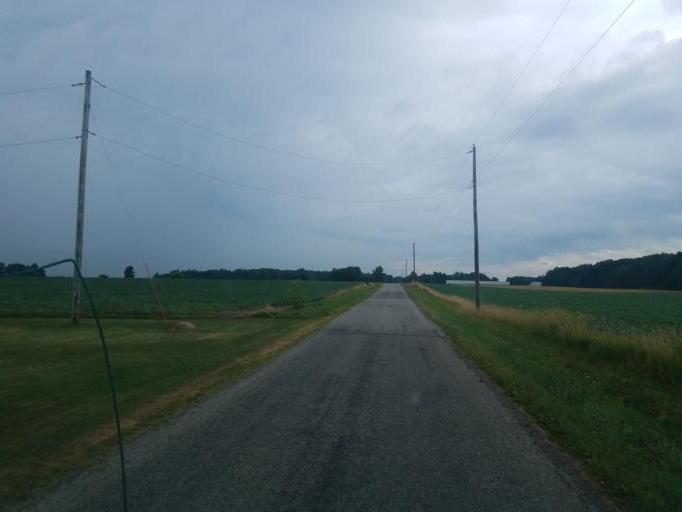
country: US
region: Ohio
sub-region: Defiance County
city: Hicksville
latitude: 41.3560
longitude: -84.8040
